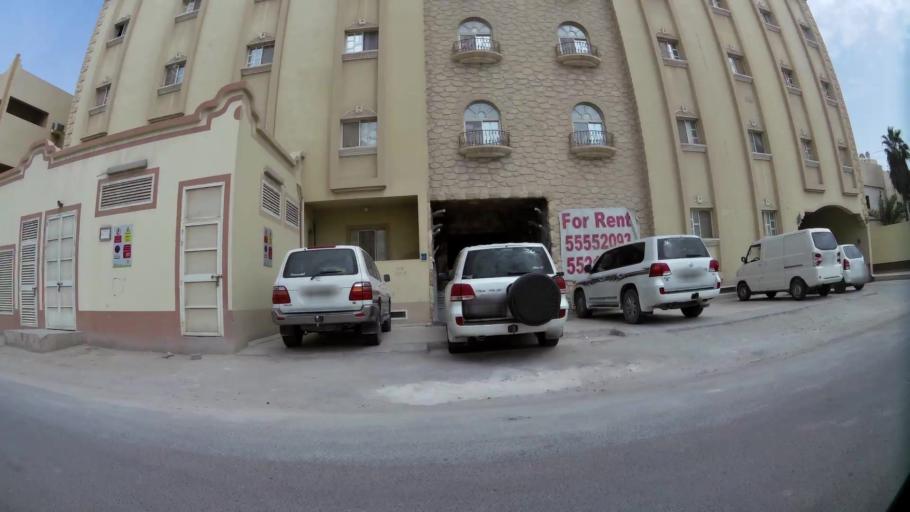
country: QA
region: Baladiyat ad Dawhah
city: Doha
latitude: 25.3075
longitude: 51.4925
